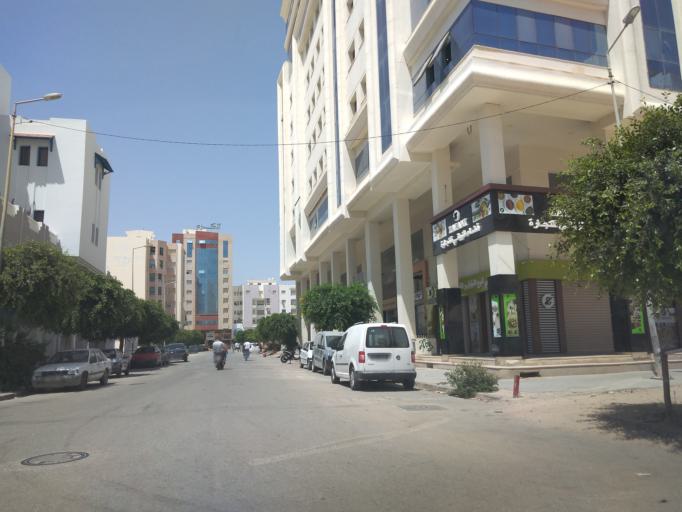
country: TN
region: Safaqis
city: Sfax
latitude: 34.7400
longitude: 10.7549
